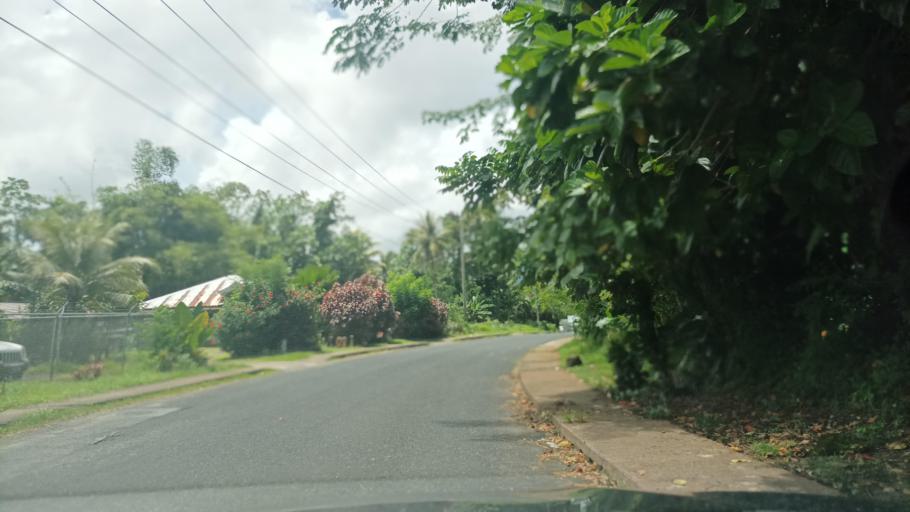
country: FM
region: Pohnpei
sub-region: Kolonia Municipality
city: Kolonia
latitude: 6.9624
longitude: 158.2121
